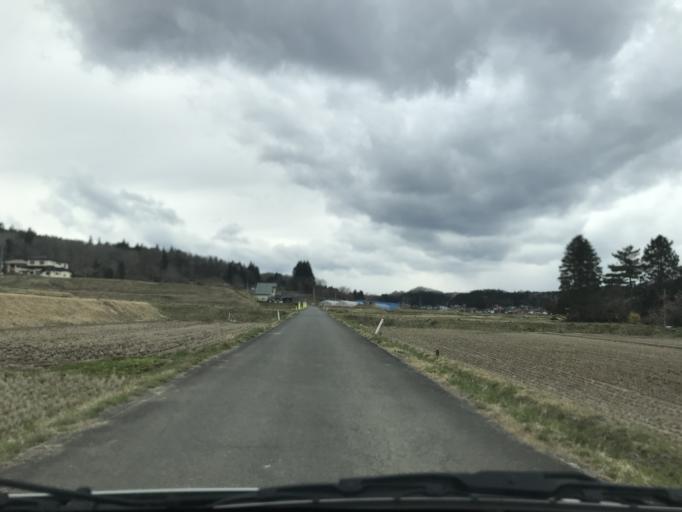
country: JP
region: Iwate
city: Ichinoseki
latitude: 38.9754
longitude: 141.0941
